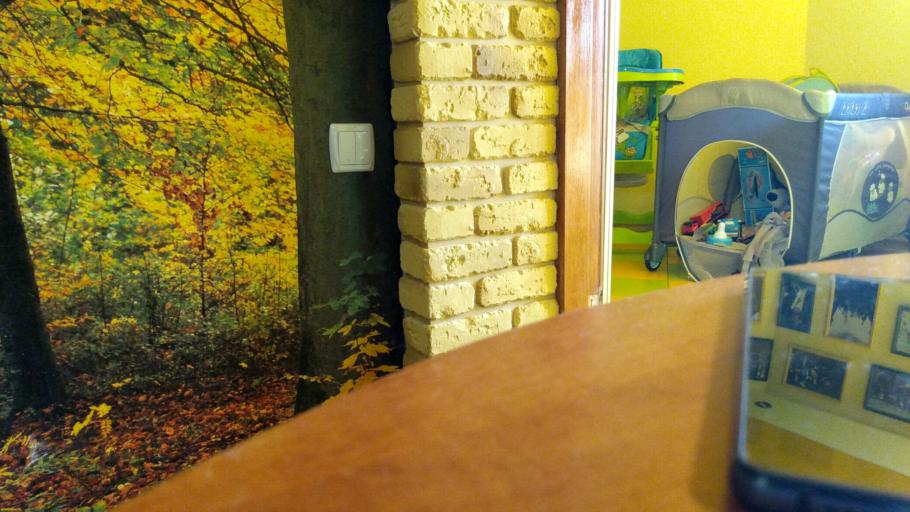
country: RU
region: Tverskaya
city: Likhoslavl'
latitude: 57.2468
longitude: 35.4342
